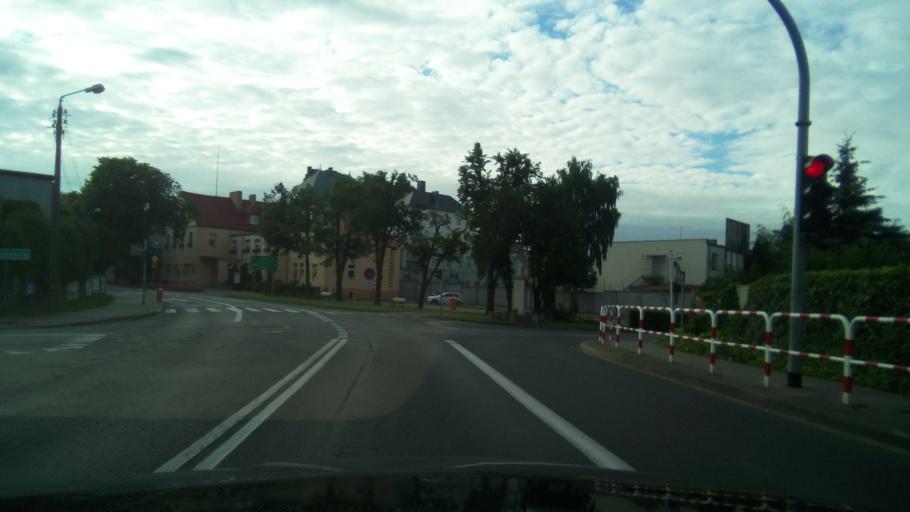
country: PL
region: Greater Poland Voivodeship
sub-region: Powiat gnieznienski
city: Witkowo
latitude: 52.4415
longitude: 17.7686
